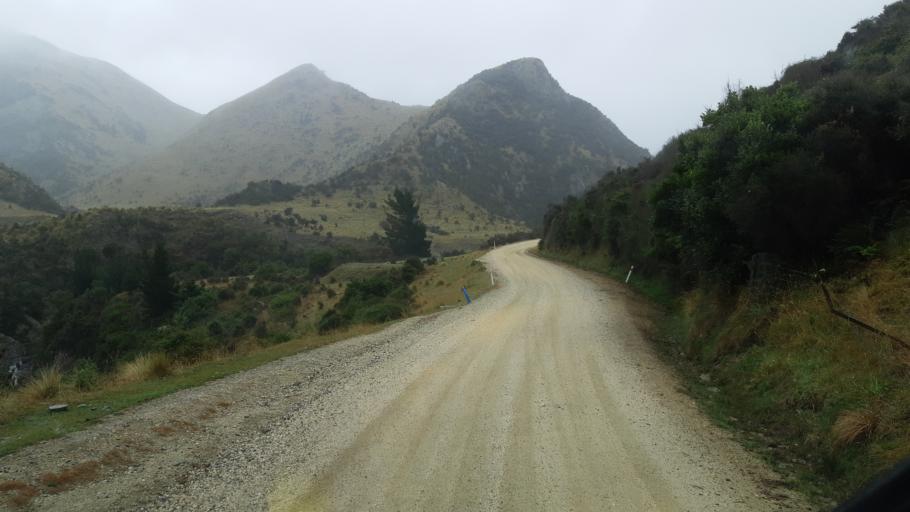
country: NZ
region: Otago
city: Oamaru
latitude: -44.9610
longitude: 170.4623
